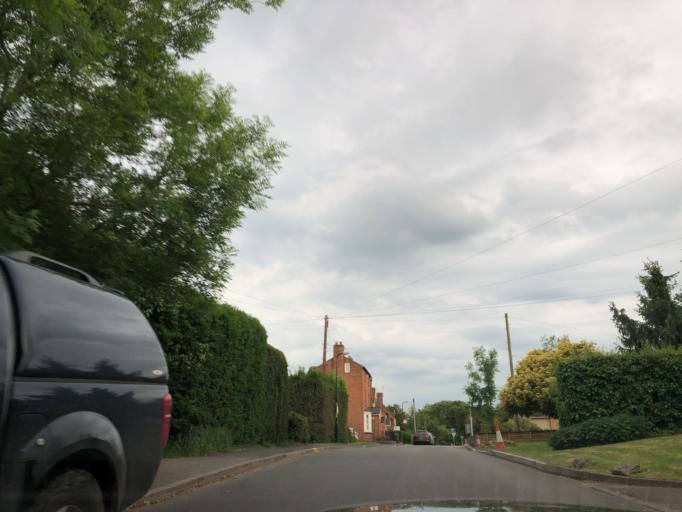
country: GB
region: England
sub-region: Warwickshire
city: Warwick
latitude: 52.2789
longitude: -1.6317
